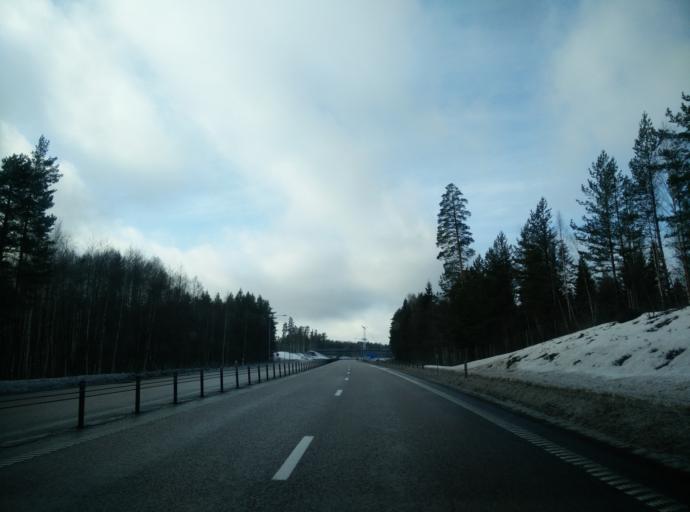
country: SE
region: Gaevleborg
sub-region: Sandvikens Kommun
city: Sandviken
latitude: 60.6257
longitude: 16.7366
